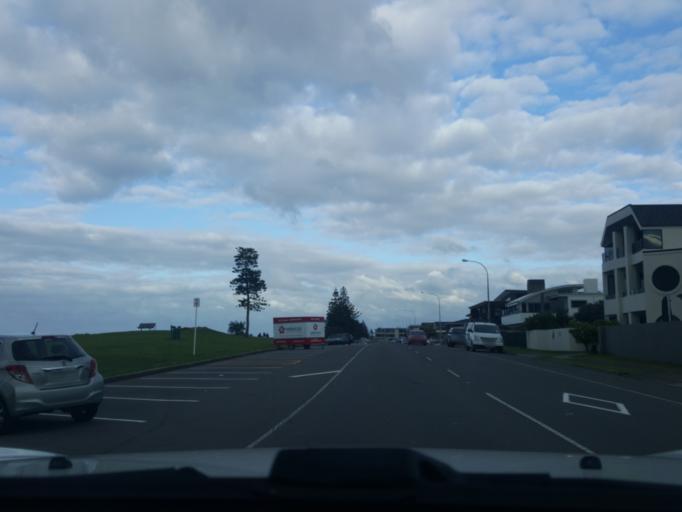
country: NZ
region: Bay of Plenty
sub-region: Tauranga City
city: Tauranga
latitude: -37.6472
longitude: 176.1990
